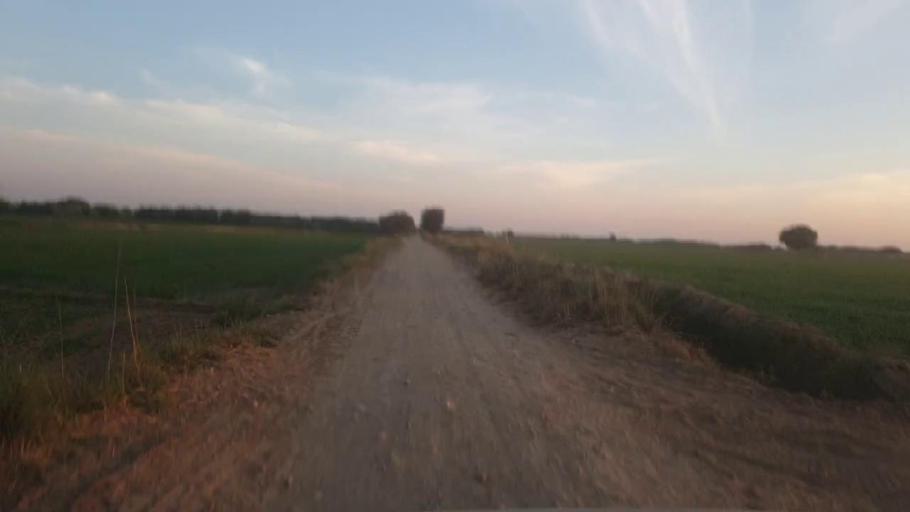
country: PK
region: Sindh
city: Hala
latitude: 25.6986
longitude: 68.3174
